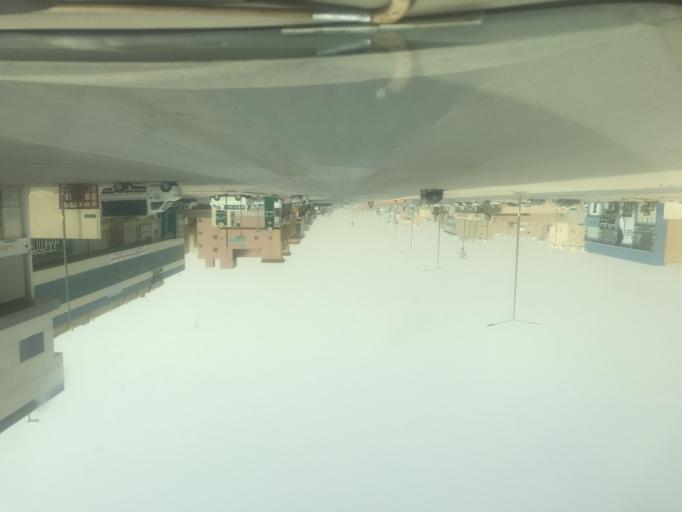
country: SA
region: Ar Riyad
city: Riyadh
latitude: 24.8054
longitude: 46.6032
